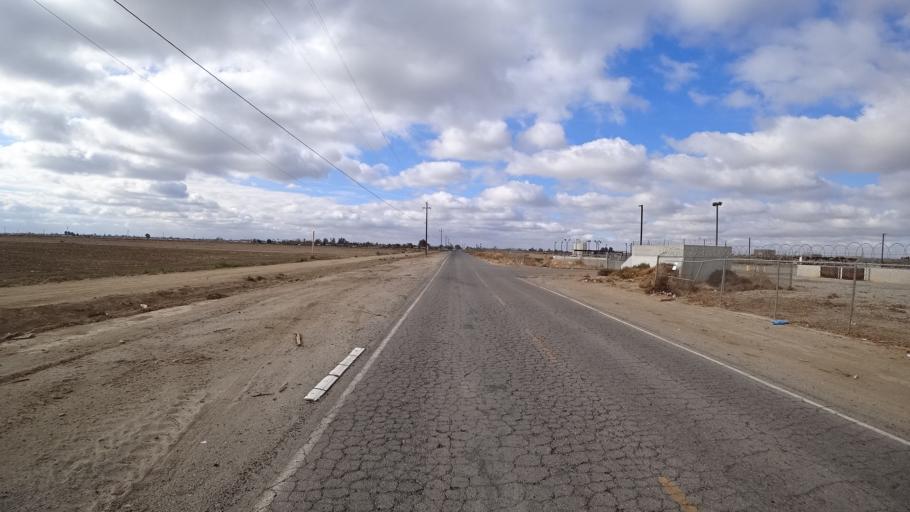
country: US
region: California
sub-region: Kern County
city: Greenfield
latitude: 35.3250
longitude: -118.9737
